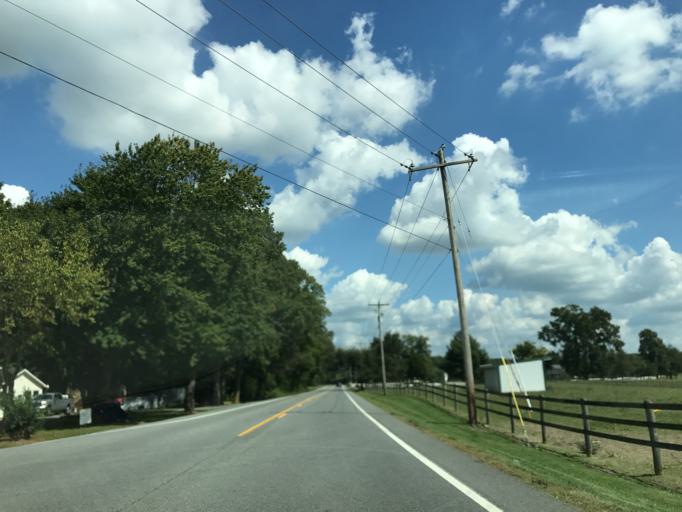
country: US
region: Maryland
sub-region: Caroline County
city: Ridgely
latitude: 39.0176
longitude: -75.9261
